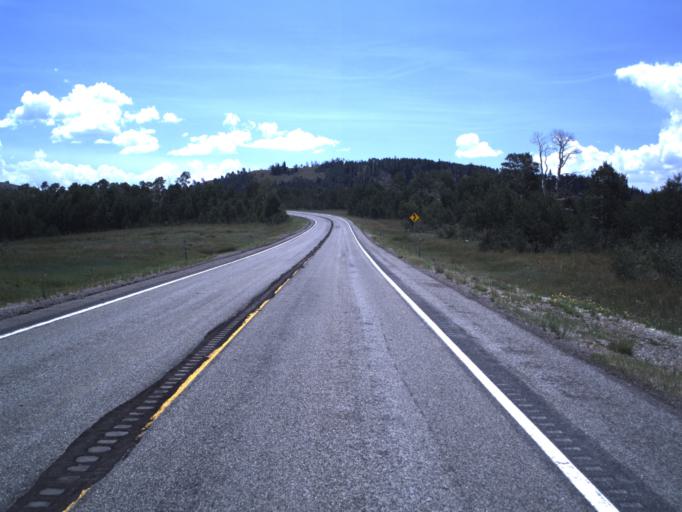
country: US
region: Utah
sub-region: Sanpete County
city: Fairview
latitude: 39.6667
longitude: -111.3275
